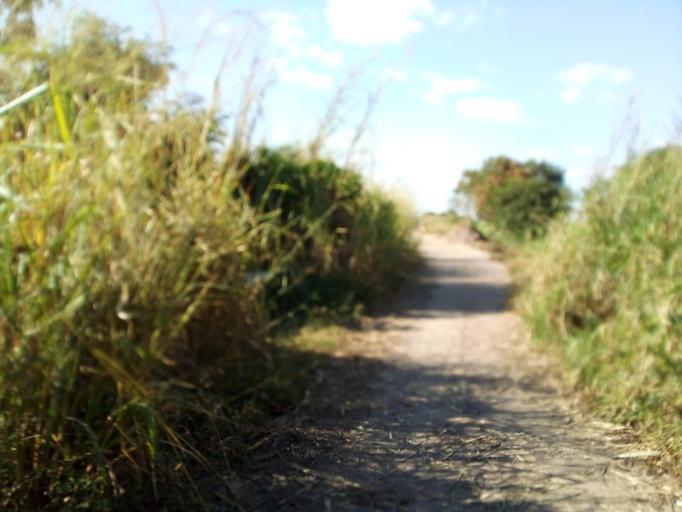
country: MZ
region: Zambezia
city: Quelimane
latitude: -17.5878
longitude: 36.8387
